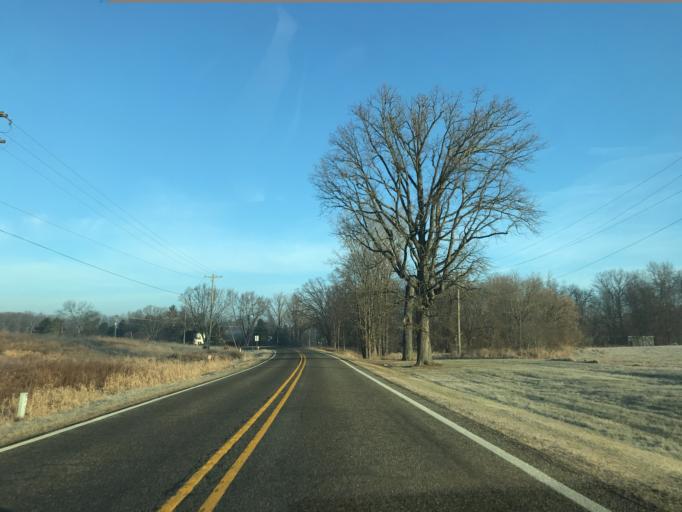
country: US
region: Michigan
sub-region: Eaton County
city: Eaton Rapids
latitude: 42.4854
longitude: -84.6010
